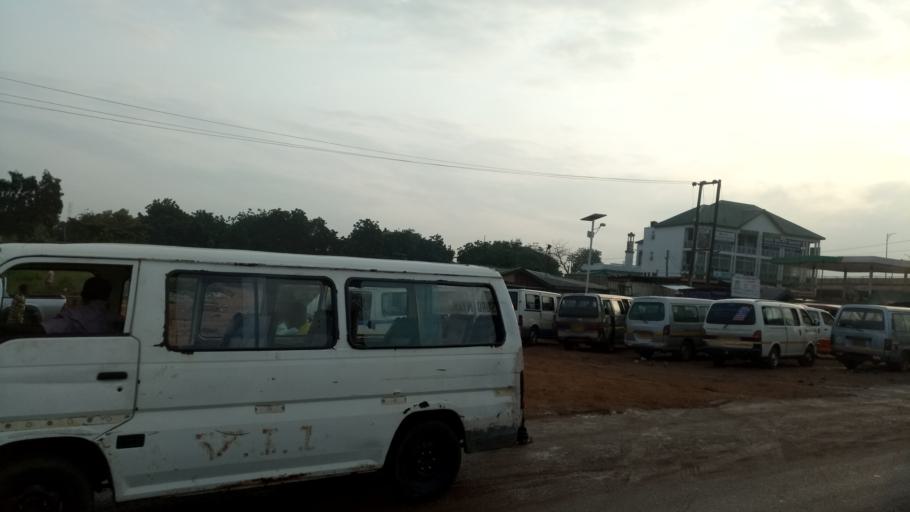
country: GH
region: Greater Accra
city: Medina Estates
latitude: 5.6673
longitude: -0.1784
